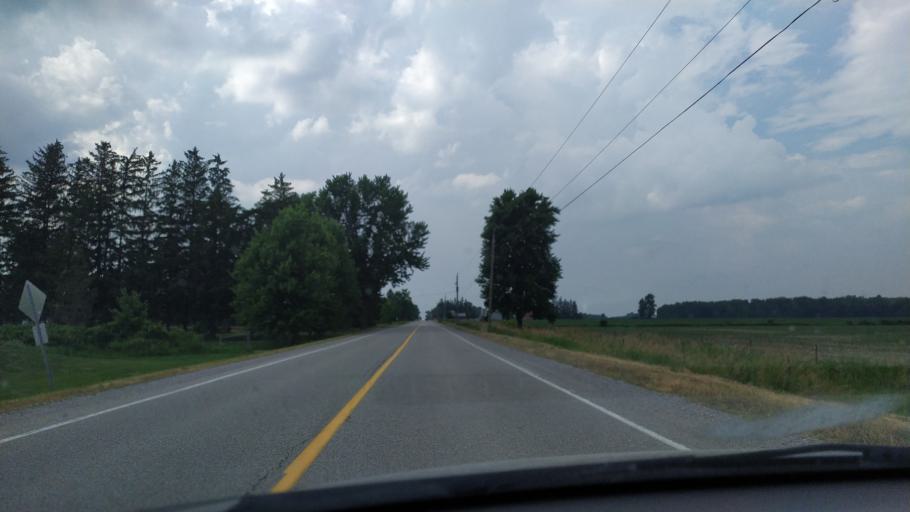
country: CA
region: Ontario
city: Dorchester
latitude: 43.1696
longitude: -81.1367
